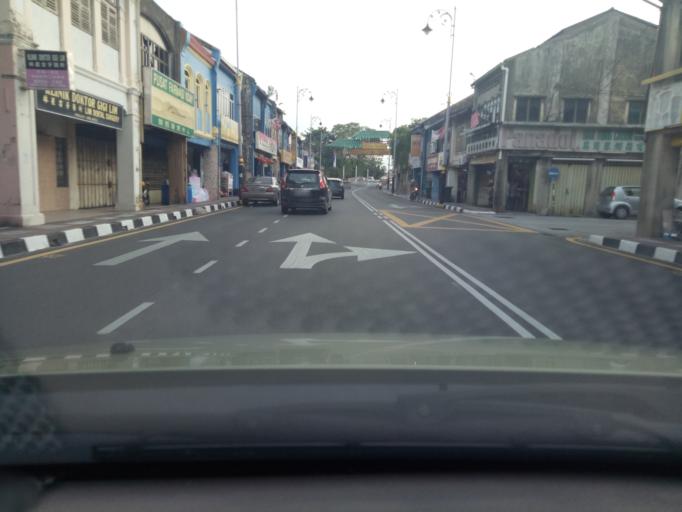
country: MY
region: Kedah
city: Alor Setar
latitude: 6.1168
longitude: 100.3642
